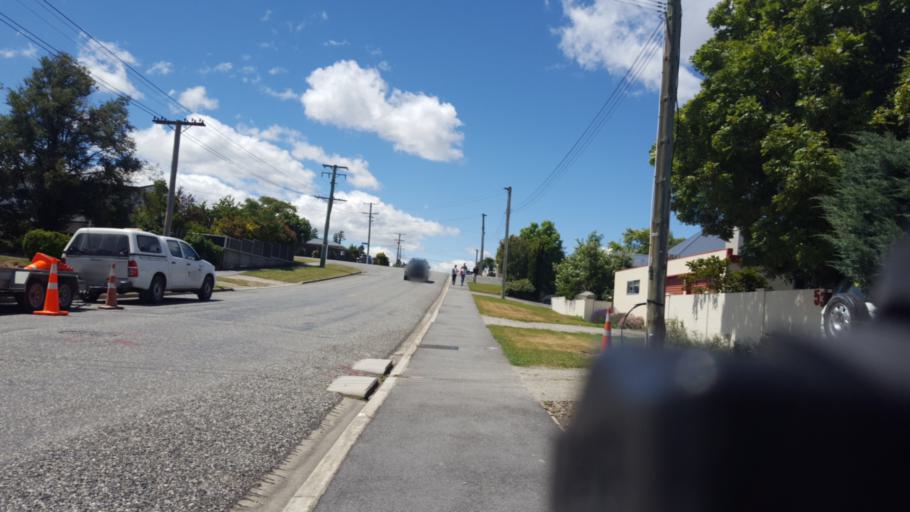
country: NZ
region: Otago
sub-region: Queenstown-Lakes District
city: Wanaka
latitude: -45.2489
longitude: 169.3938
